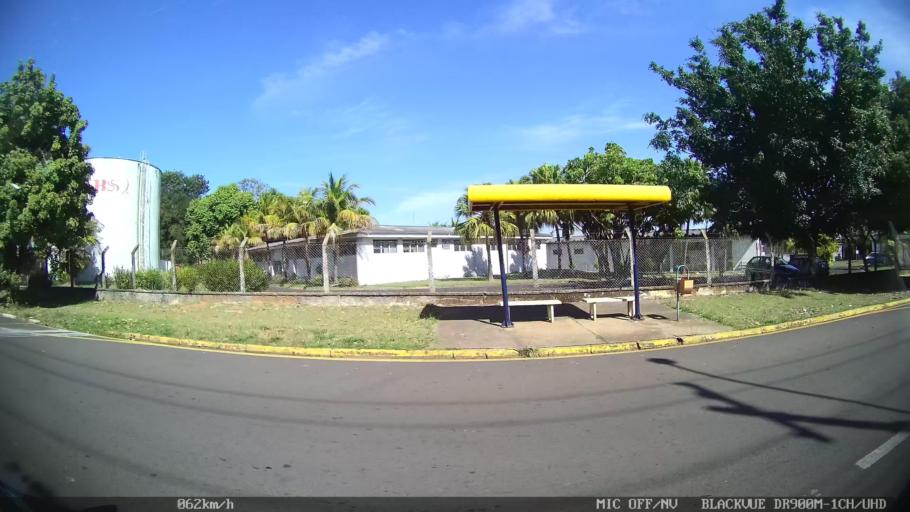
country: BR
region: Sao Paulo
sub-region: Franca
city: Franca
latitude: -20.5520
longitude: -47.4460
